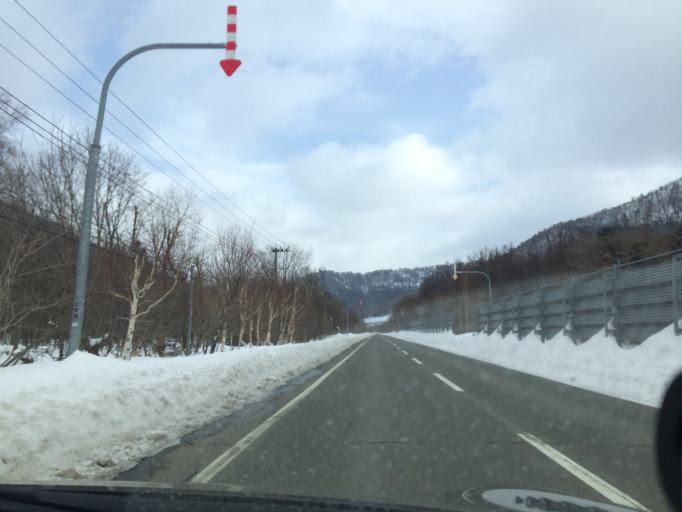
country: JP
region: Hokkaido
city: Shimo-furano
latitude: 43.0575
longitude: 142.5688
